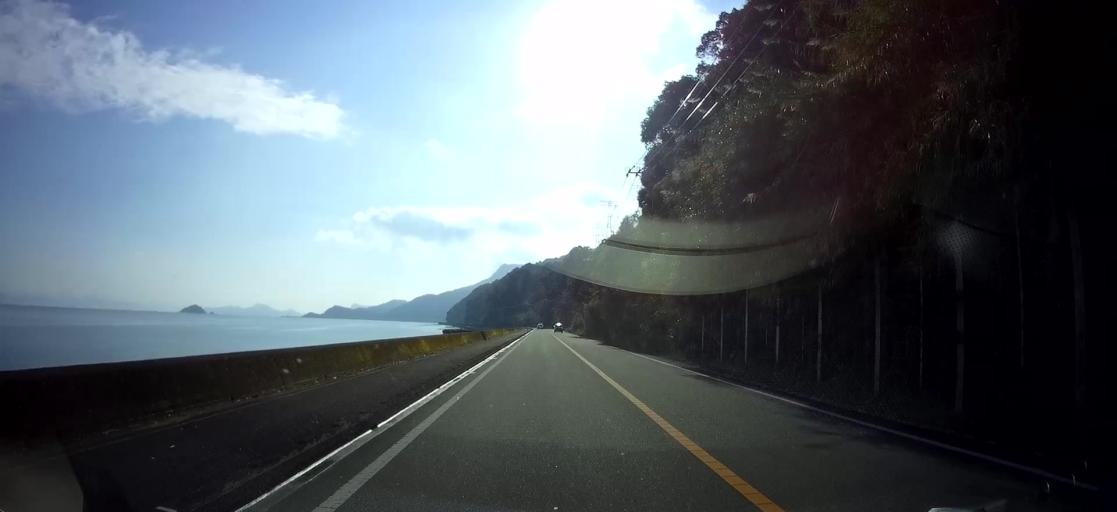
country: JP
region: Kumamoto
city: Yatsushiro
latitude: 32.5004
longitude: 130.4475
